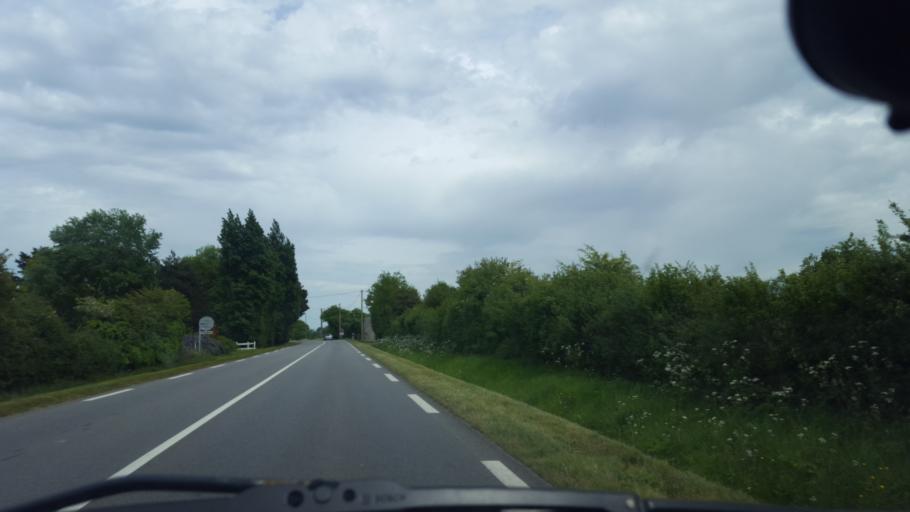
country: FR
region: Pays de la Loire
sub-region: Departement de la Loire-Atlantique
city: Saint-Meme-le-Tenu
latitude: 46.9901
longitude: -1.7880
